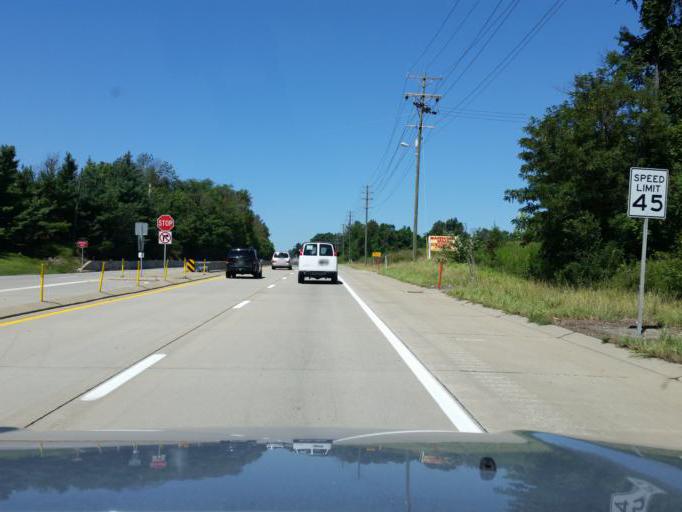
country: US
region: Pennsylvania
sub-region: Westmoreland County
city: Delmont
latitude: 40.4102
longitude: -79.6188
